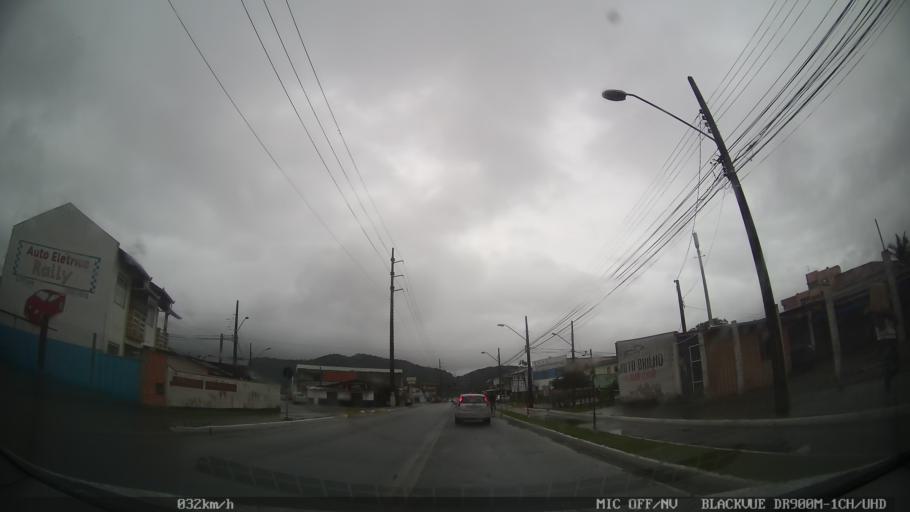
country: BR
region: Santa Catarina
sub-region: Itajai
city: Itajai
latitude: -26.9252
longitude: -48.6955
